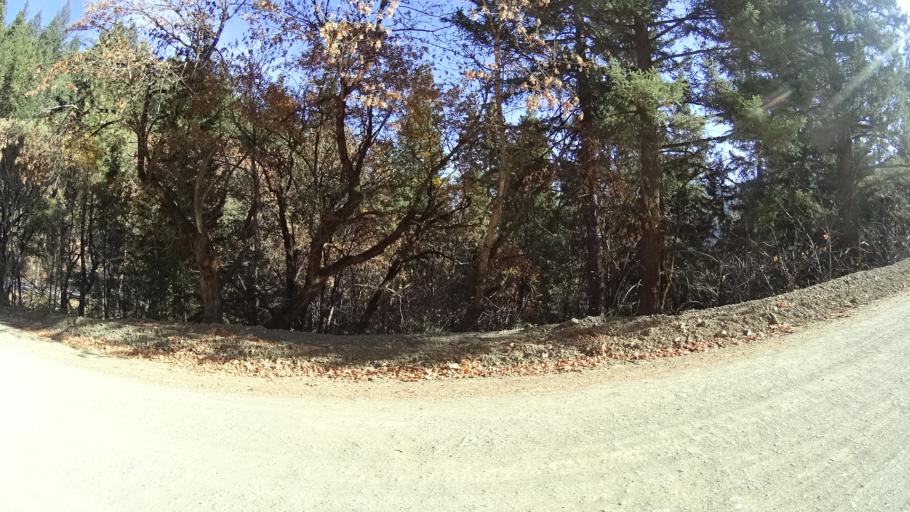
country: US
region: California
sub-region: Siskiyou County
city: Yreka
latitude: 41.7316
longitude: -122.7278
